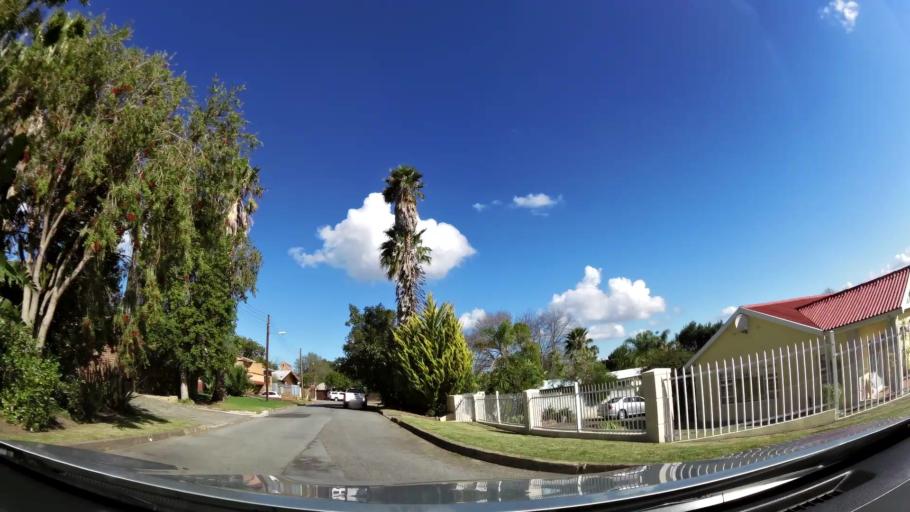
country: ZA
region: Western Cape
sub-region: Eden District Municipality
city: George
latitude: -33.9675
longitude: 22.4470
